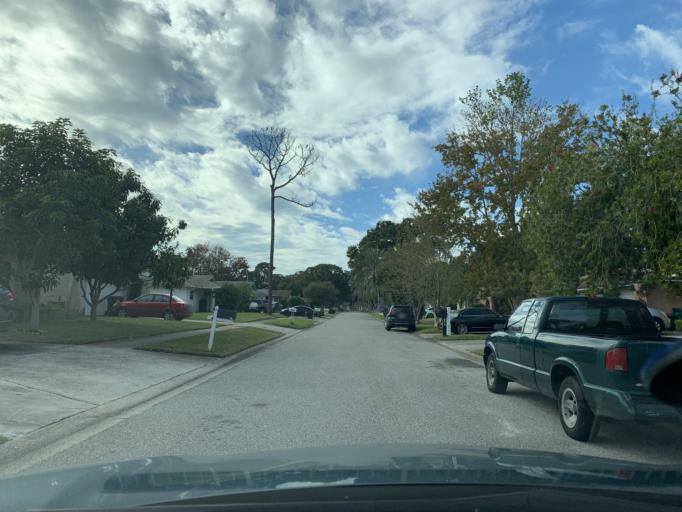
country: US
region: Florida
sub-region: Pinellas County
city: Kenneth City
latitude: 27.8275
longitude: -82.7378
